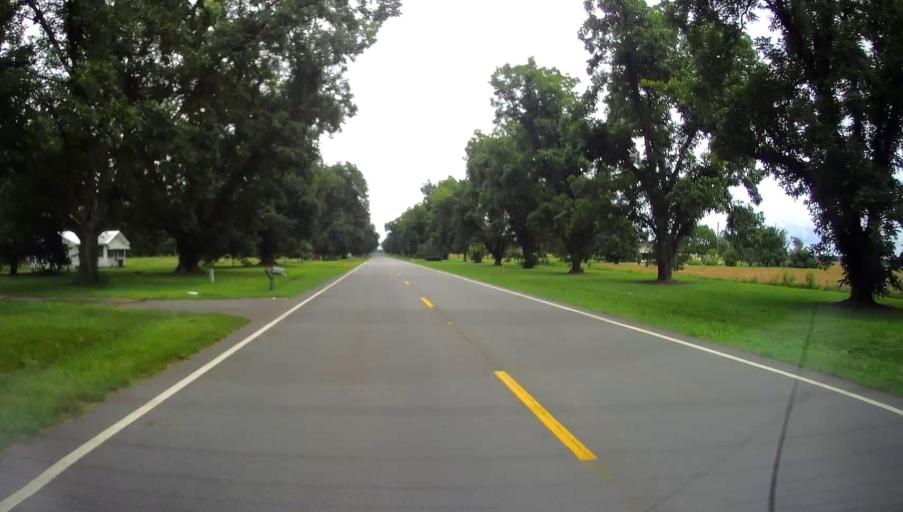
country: US
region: Georgia
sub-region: Macon County
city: Montezuma
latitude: 32.2931
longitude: -83.9708
